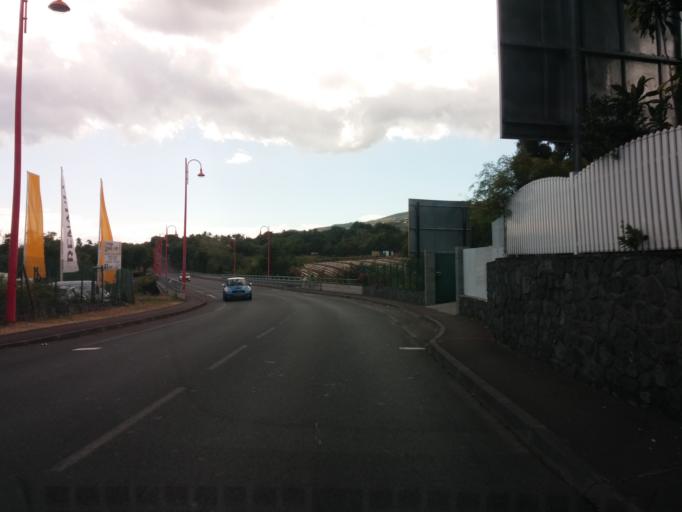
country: RE
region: Reunion
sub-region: Reunion
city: La Possession
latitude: -20.9405
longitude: 55.3305
